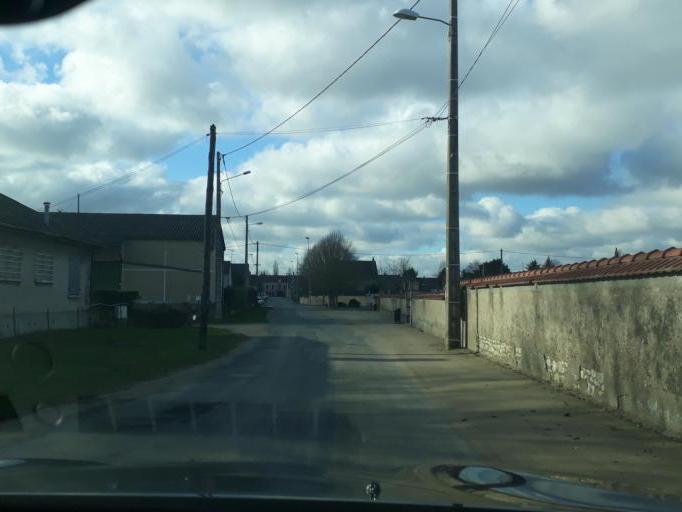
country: FR
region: Centre
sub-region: Departement du Loiret
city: Chevilly
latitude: 48.0282
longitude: 1.8787
